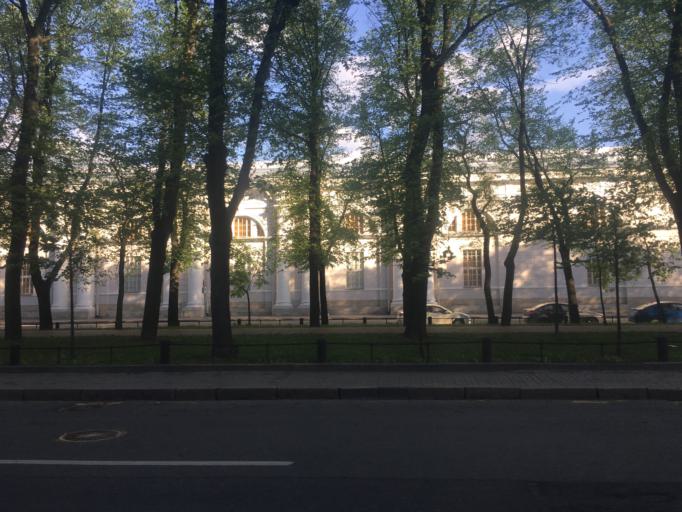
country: RU
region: St.-Petersburg
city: Saint Petersburg
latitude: 59.9345
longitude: 30.3017
